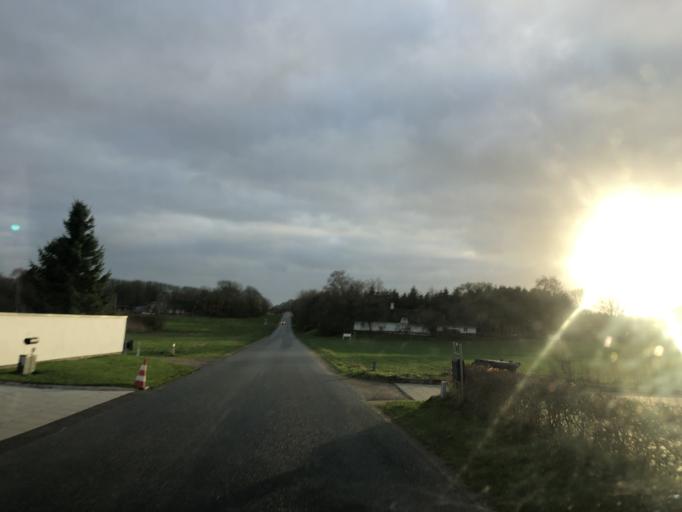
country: DK
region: Central Jutland
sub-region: Viborg Kommune
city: Viborg
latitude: 56.5009
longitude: 9.3453
